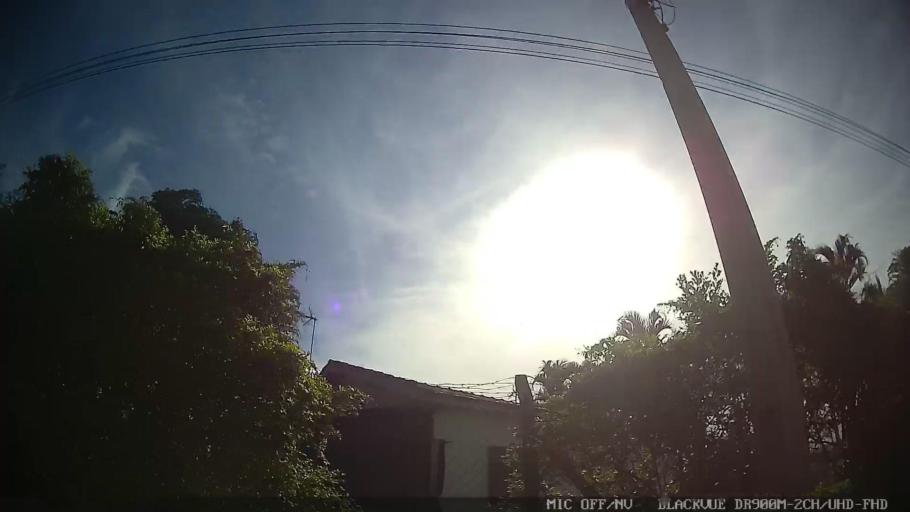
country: BR
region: Sao Paulo
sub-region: Jaguariuna
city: Jaguariuna
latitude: -22.6470
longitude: -47.0405
